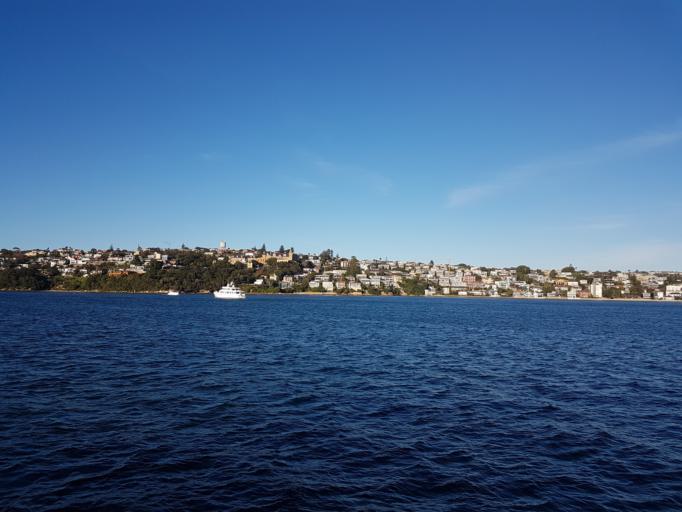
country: AU
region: New South Wales
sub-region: Woollahra
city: Point Piper
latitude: -33.8645
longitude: 151.2612
